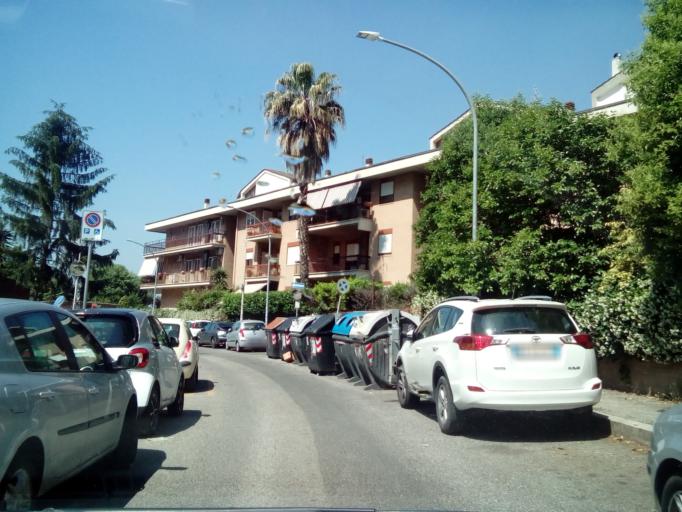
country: IT
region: Latium
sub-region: Citta metropolitana di Roma Capitale
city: Rome
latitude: 41.8901
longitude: 12.5851
